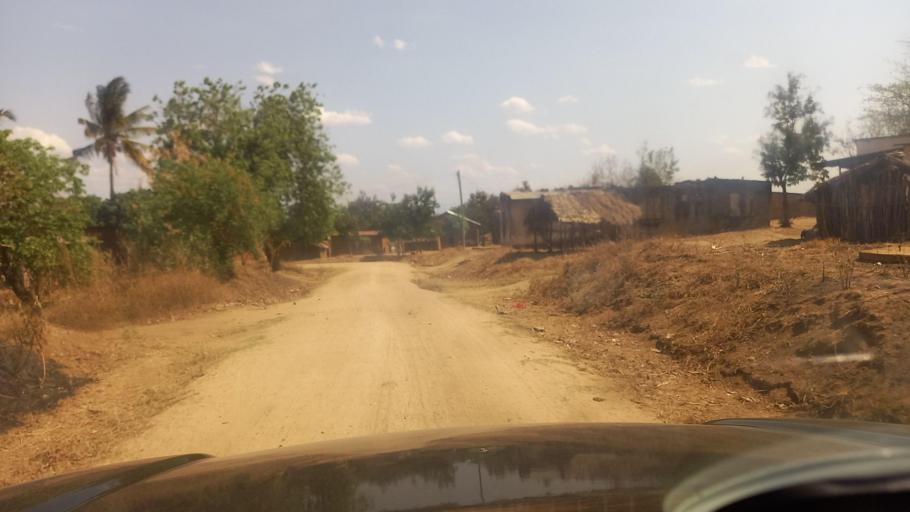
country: TZ
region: Morogoro
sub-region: Kilosa
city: Magole
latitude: -6.3212
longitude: 37.3731
